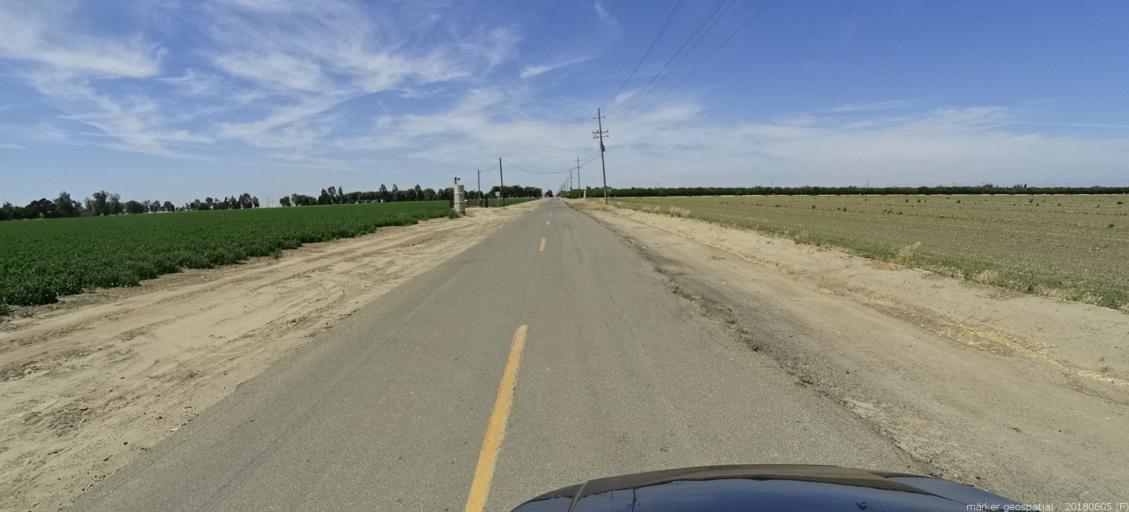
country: US
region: California
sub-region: Merced County
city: Dos Palos
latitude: 37.0942
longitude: -120.4734
